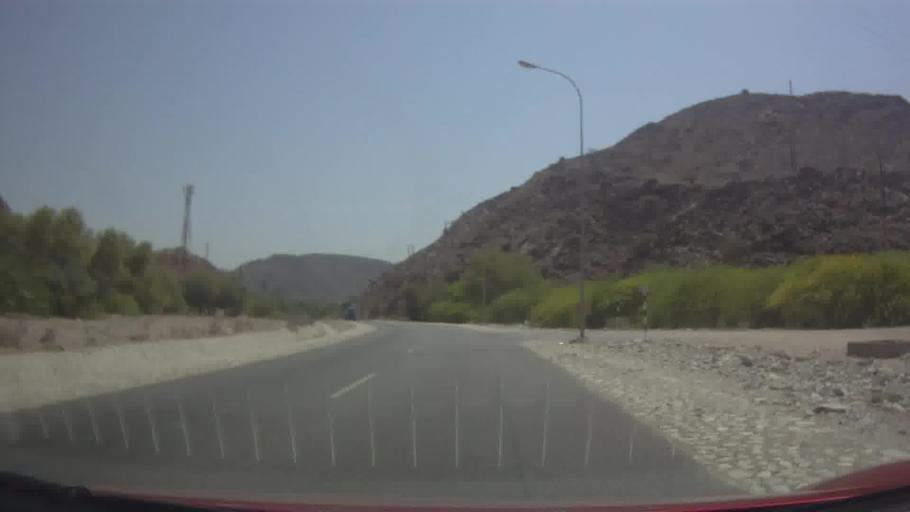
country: OM
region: Muhafazat Masqat
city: Muscat
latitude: 23.5090
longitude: 58.6500
